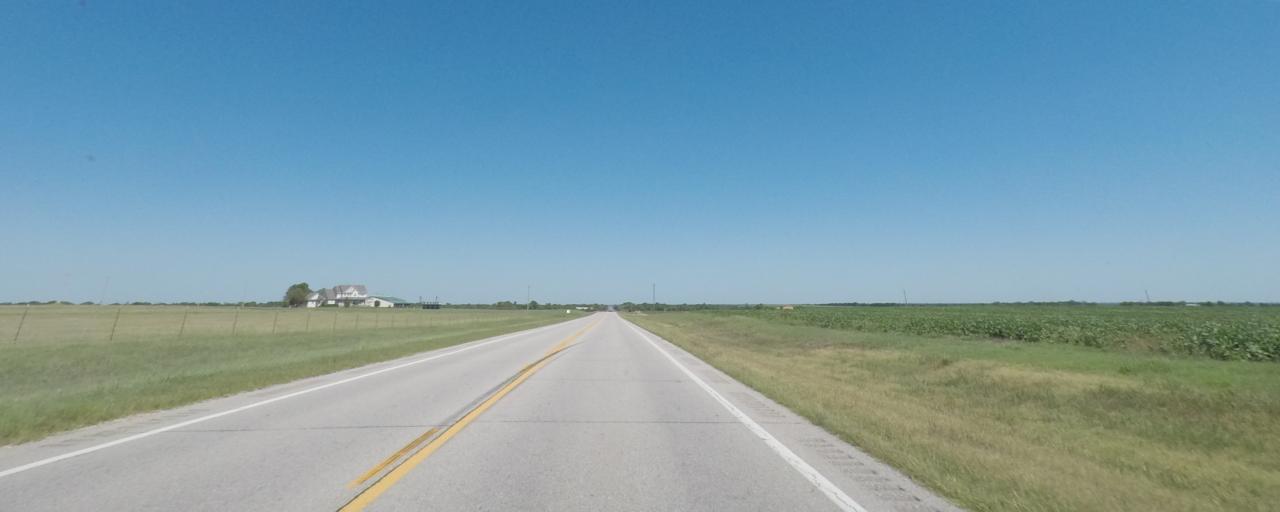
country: US
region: Kansas
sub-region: Sumner County
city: Wellington
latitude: 37.3596
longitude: -97.3851
